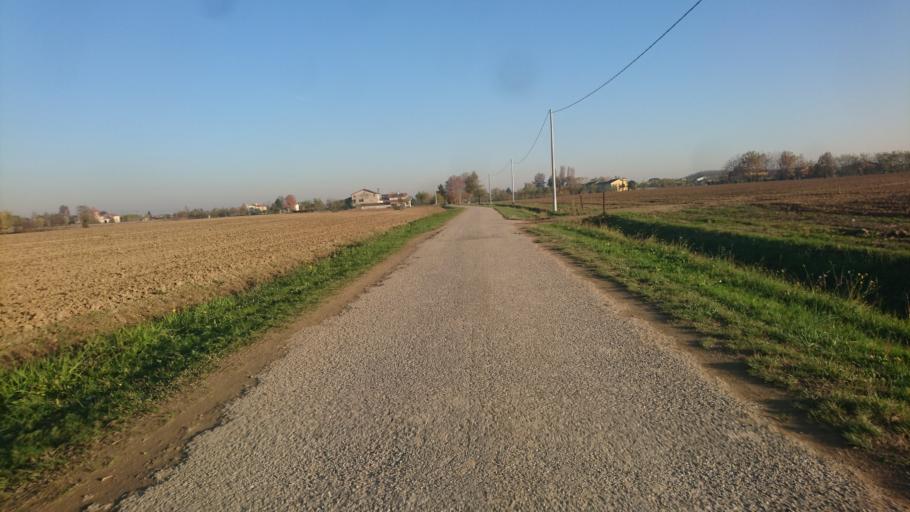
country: IT
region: Veneto
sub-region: Provincia di Padova
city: Bosco
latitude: 45.4460
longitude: 11.8013
